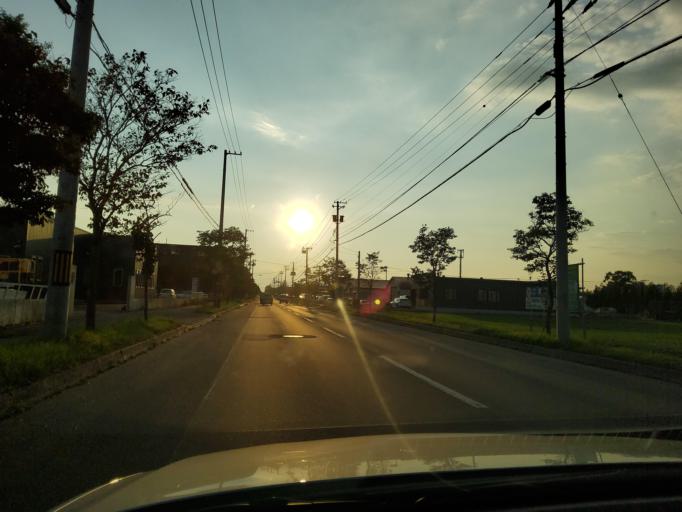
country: JP
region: Hokkaido
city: Obihiro
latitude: 42.9333
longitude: 143.1513
